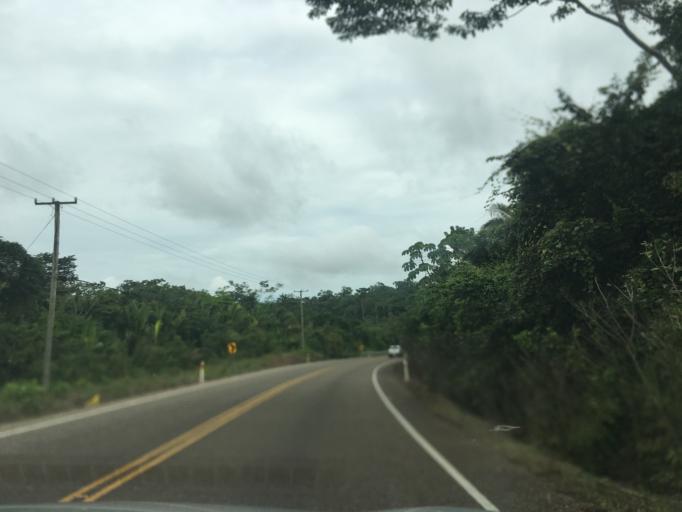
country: BZ
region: Cayo
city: Belmopan
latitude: 17.2041
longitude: -88.7745
